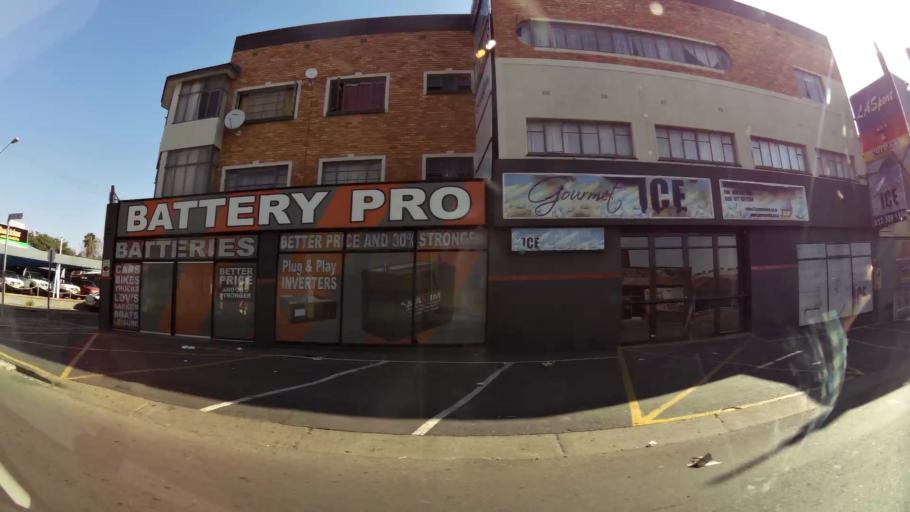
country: ZA
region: Gauteng
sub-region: City of Tshwane Metropolitan Municipality
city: Pretoria
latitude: -25.7236
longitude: 28.2033
